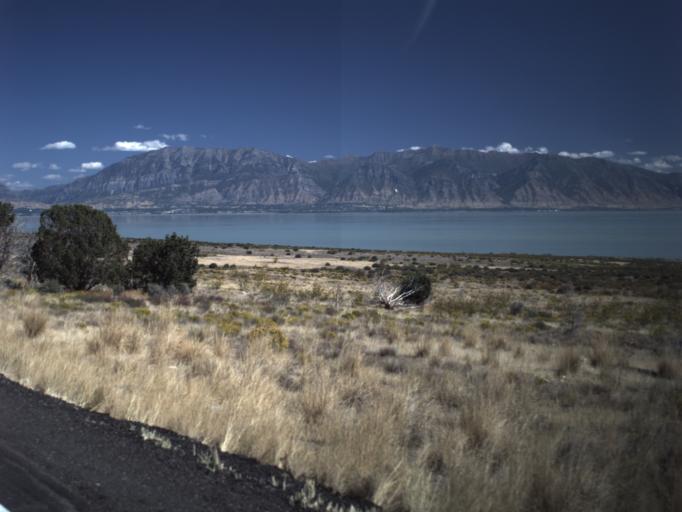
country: US
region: Utah
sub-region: Utah County
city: Saratoga Springs
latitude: 40.2204
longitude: -111.8809
